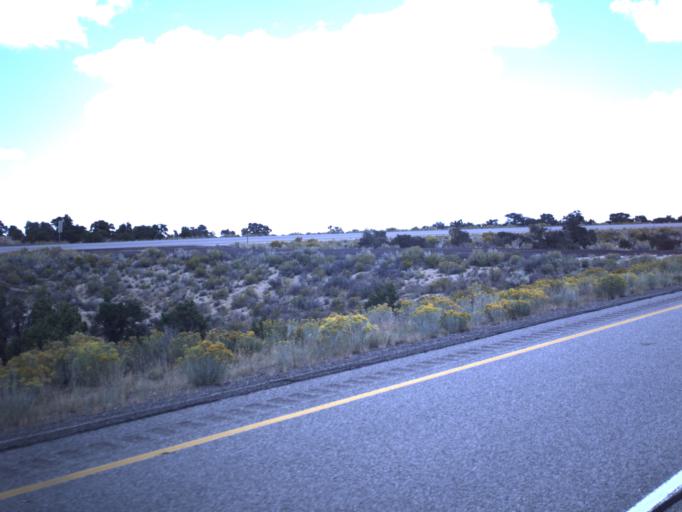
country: US
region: Utah
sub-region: Emery County
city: Ferron
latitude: 38.8639
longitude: -110.8516
